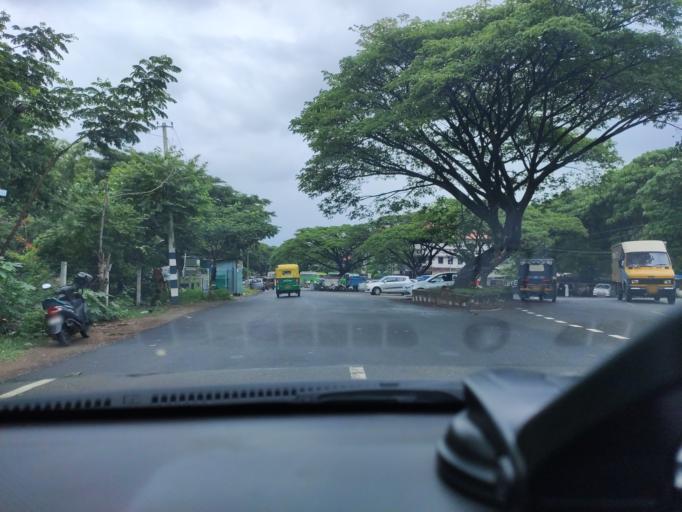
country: IN
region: Kerala
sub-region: Ernakulam
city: Elur
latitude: 10.0224
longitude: 76.3335
